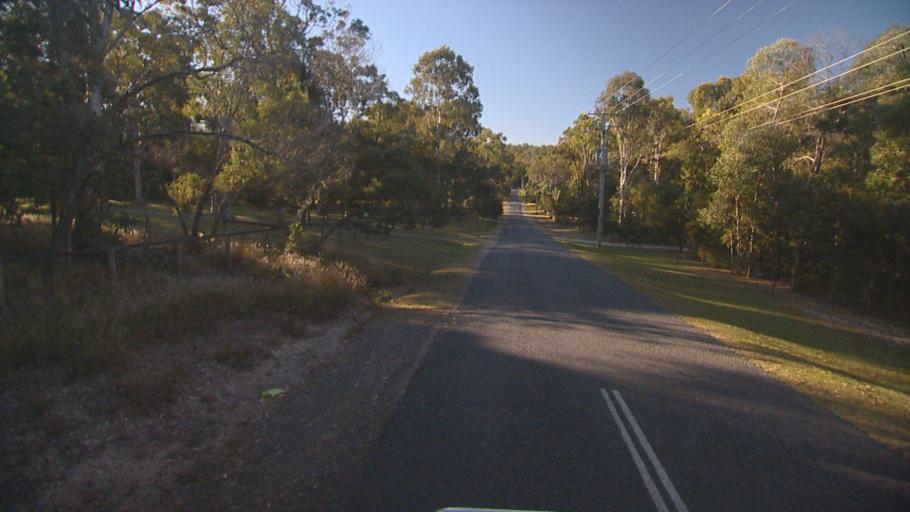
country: AU
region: Queensland
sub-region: Logan
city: Chambers Flat
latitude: -27.7726
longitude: 153.1294
